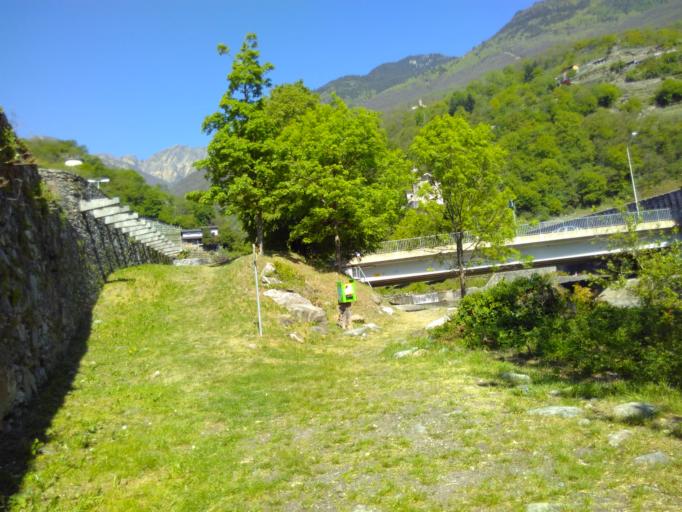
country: CH
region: Ticino
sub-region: Bellinzona District
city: Sementina
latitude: 46.1858
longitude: 8.9933
